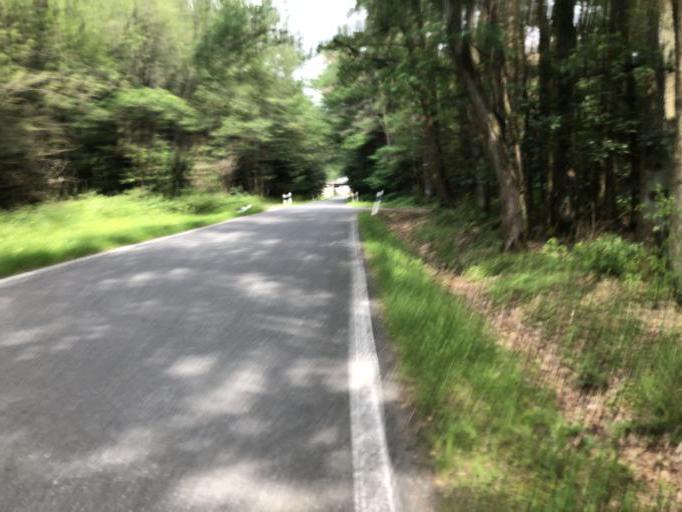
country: DE
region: Bavaria
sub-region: Regierungsbezirk Mittelfranken
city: Obermichelbach
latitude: 49.5707
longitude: 10.9329
